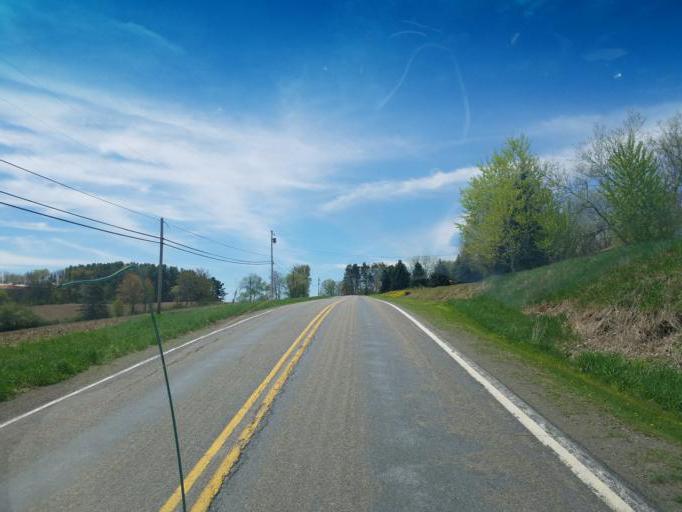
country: US
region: Pennsylvania
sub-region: Tioga County
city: Wellsboro
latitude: 41.7065
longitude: -77.3879
